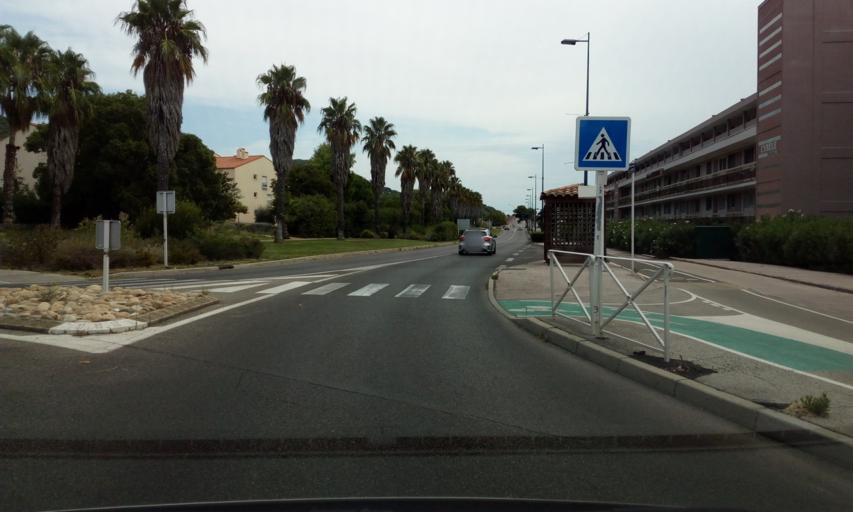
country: FR
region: Provence-Alpes-Cote d'Azur
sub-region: Departement du Var
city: Carqueiranne
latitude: 43.0912
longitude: 6.0805
